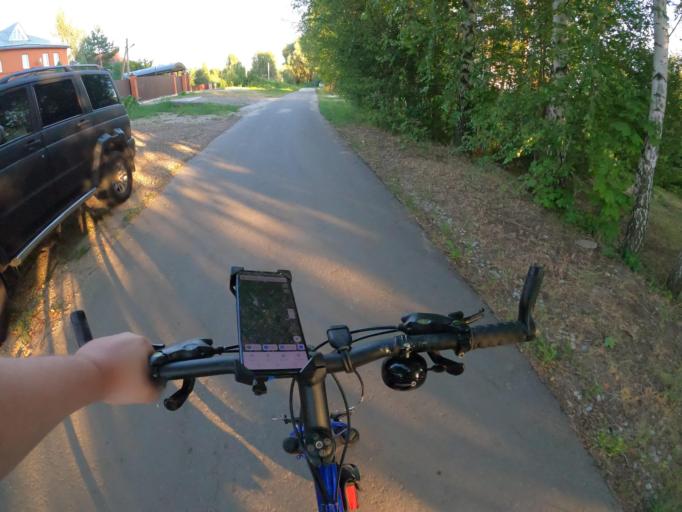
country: RU
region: Moskovskaya
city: Beloozerskiy
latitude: 55.4643
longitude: 38.4226
